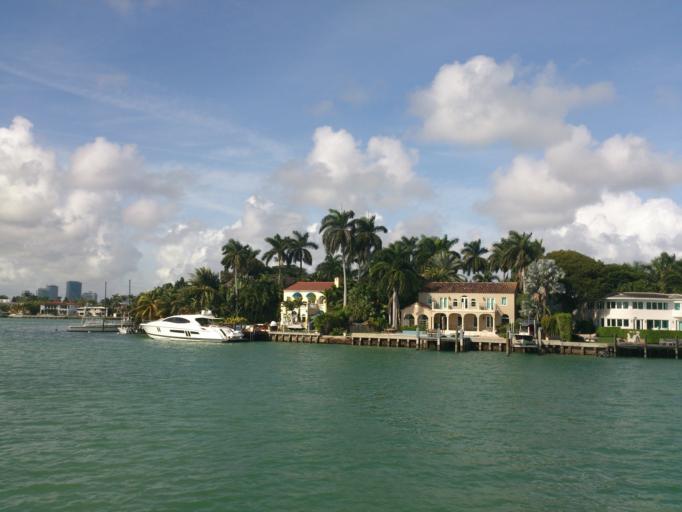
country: US
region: Florida
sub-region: Miami-Dade County
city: Miami Beach
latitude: 25.7873
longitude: -80.1622
